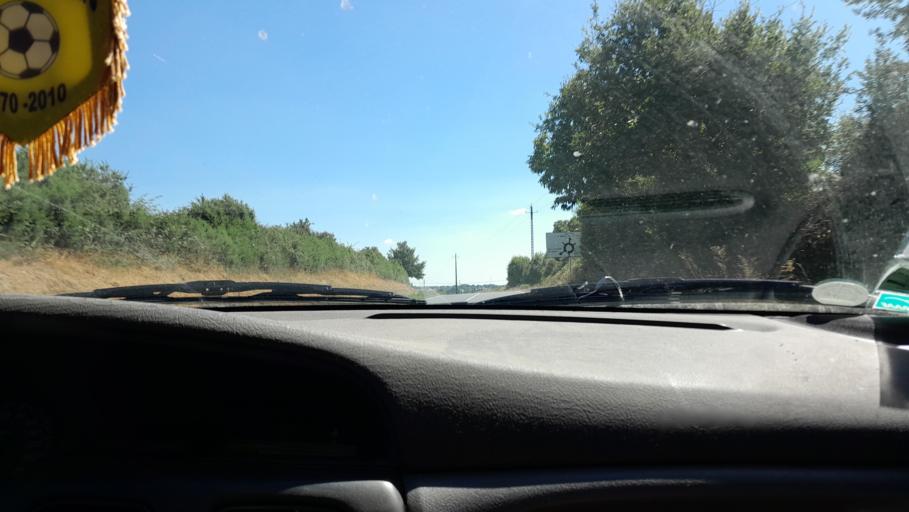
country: FR
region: Pays de la Loire
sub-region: Departement de la Loire-Atlantique
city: Saint-Mars-la-Jaille
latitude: 47.5372
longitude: -1.1871
